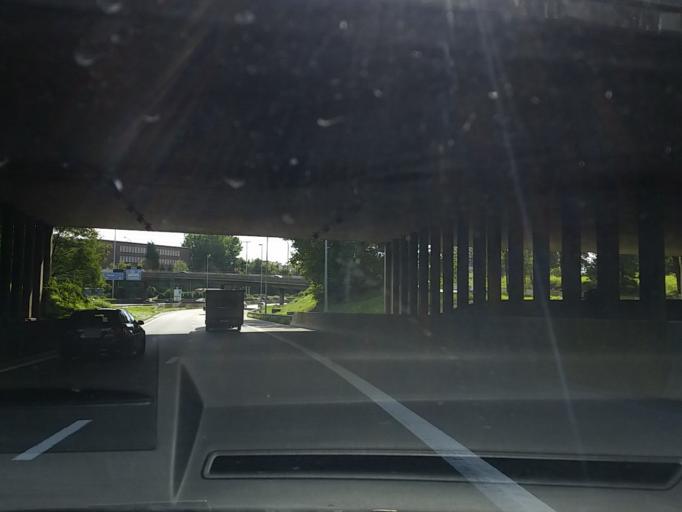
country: BE
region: Flanders
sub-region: Provincie Antwerpen
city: Borsbeek
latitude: 51.2163
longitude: 4.4483
